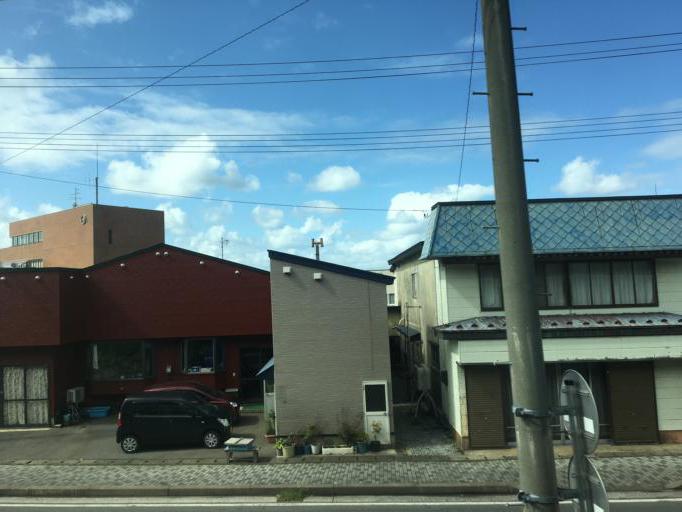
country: JP
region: Akita
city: Noshiromachi
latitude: 40.6482
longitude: 139.9284
